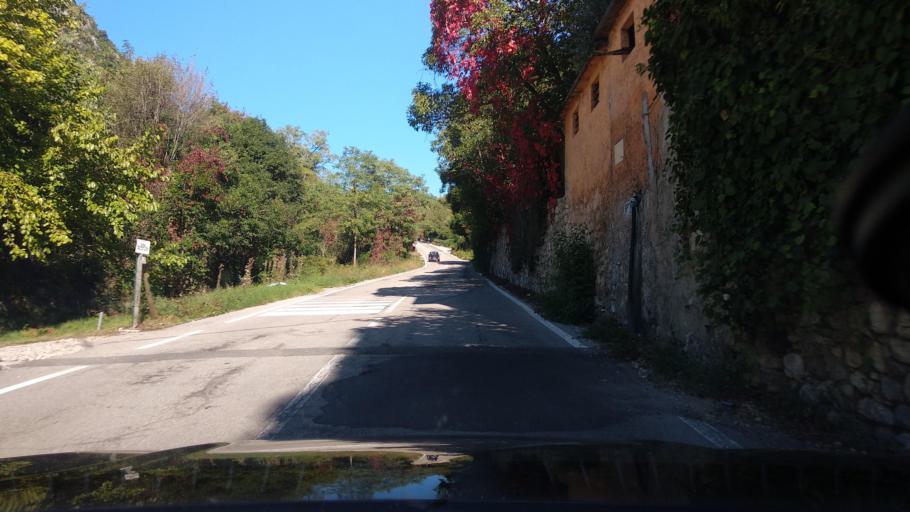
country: IT
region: Veneto
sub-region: Provincia di Verona
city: Garda
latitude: 45.5835
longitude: 10.7011
